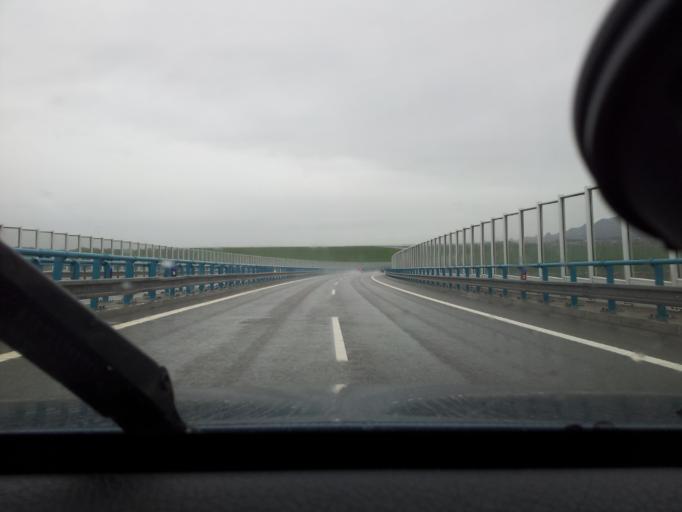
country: SK
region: Nitriansky
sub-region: Okres Nitra
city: Nitra
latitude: 48.3167
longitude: 18.1843
